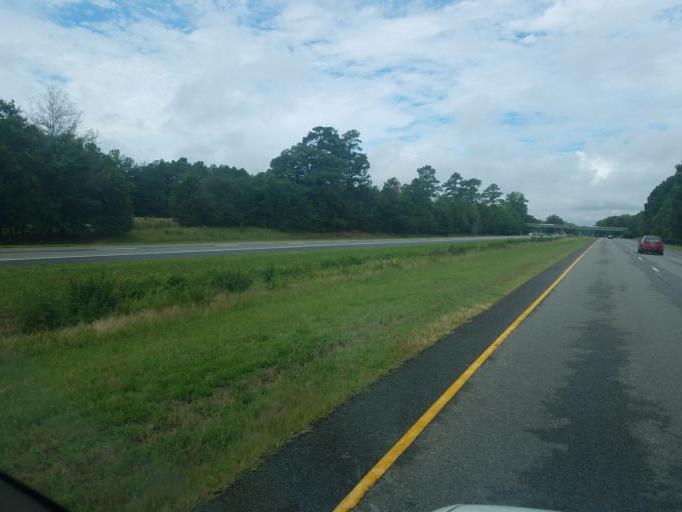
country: US
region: Virginia
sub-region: Henrico County
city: Sandston
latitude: 37.5227
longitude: -77.2753
